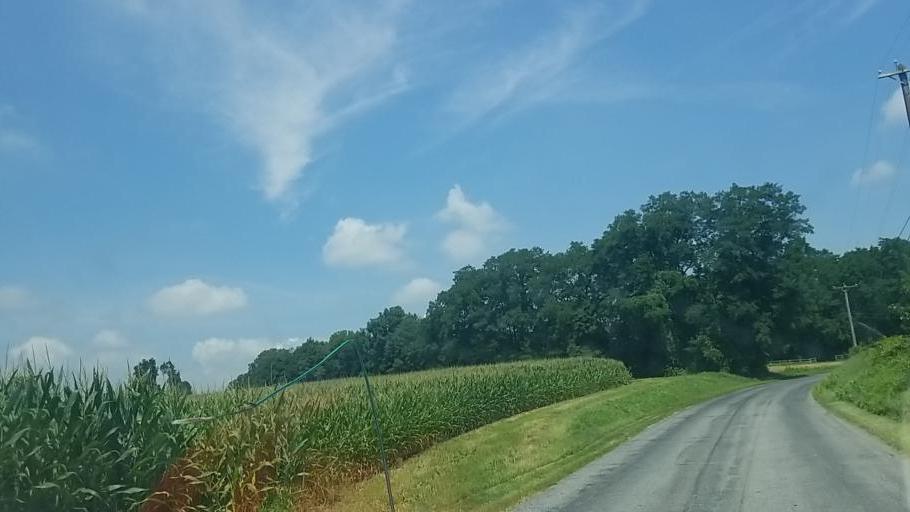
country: US
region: Pennsylvania
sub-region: Chester County
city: Atglen
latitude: 39.8754
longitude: -75.9756
